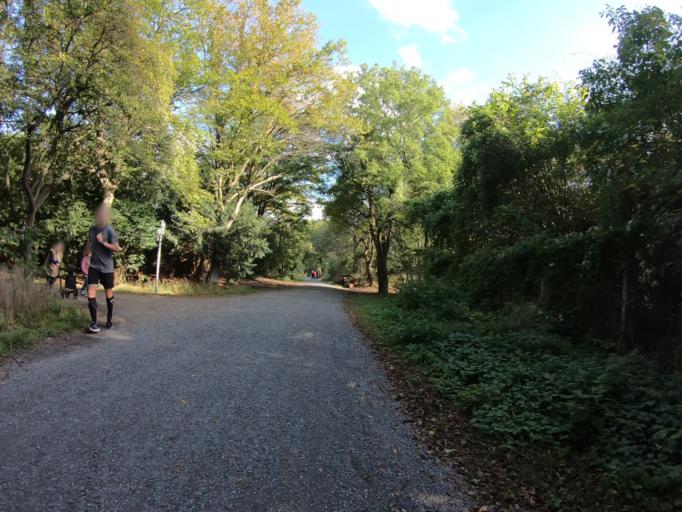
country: DE
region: Lower Saxony
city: Wolfsburg
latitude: 52.4161
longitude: 10.7698
